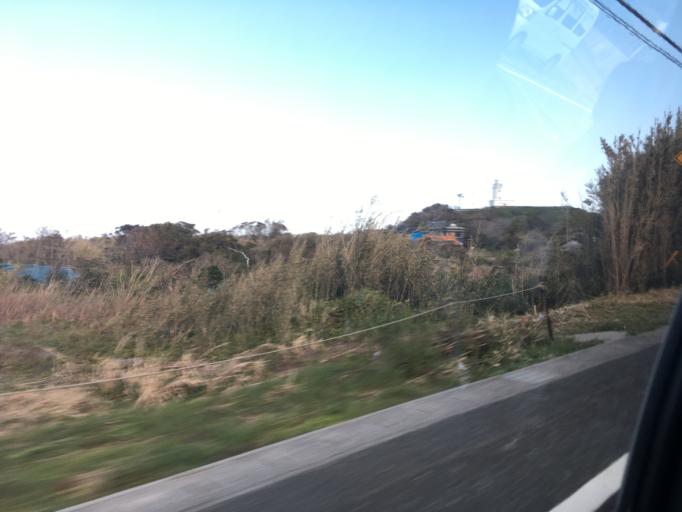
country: JP
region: Chiba
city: Tateyama
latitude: 34.9729
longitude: 139.7578
